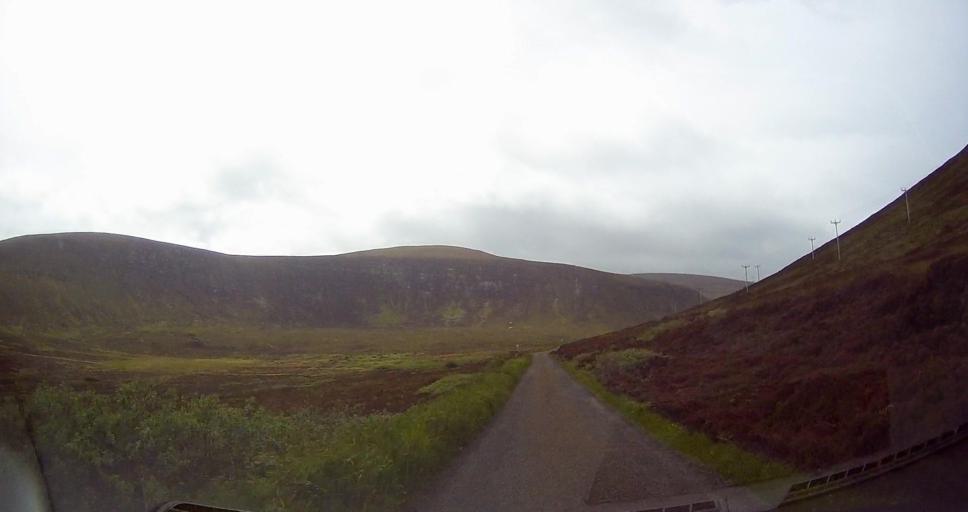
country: GB
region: Scotland
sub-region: Orkney Islands
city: Stromness
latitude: 58.8939
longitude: -3.3143
